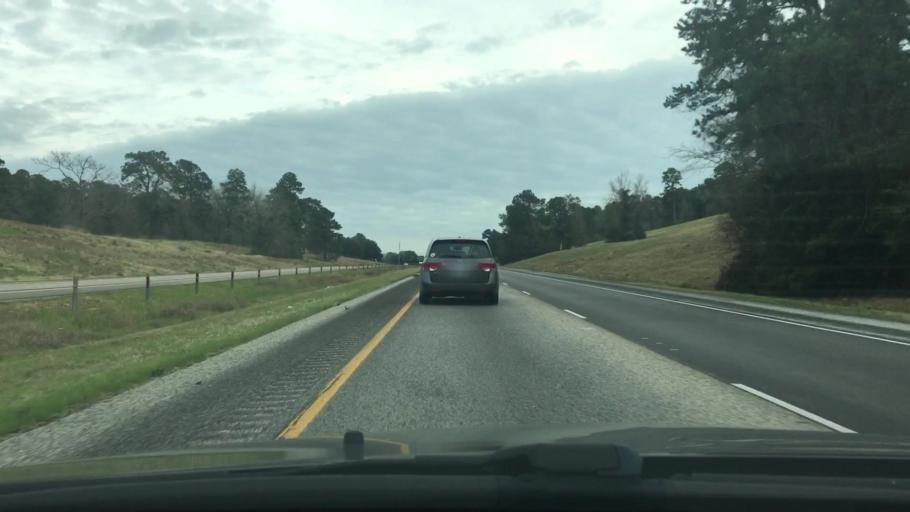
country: US
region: Texas
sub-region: Walker County
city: Huntsville
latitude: 30.8190
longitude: -95.7014
